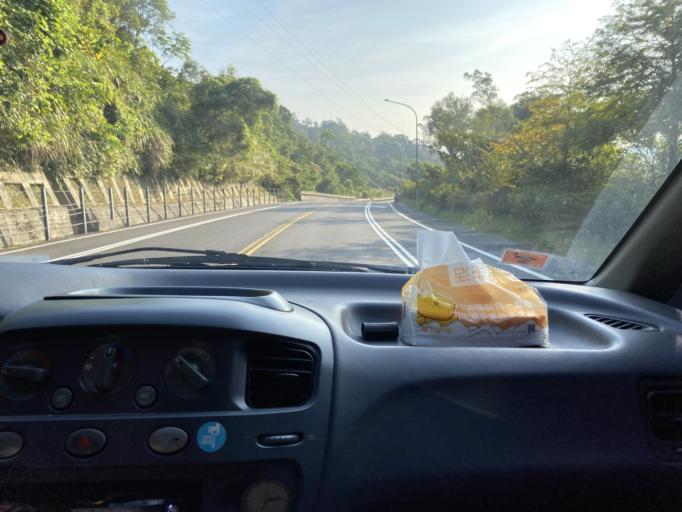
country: TW
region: Taiwan
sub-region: Keelung
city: Keelung
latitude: 25.0202
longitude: 121.8077
